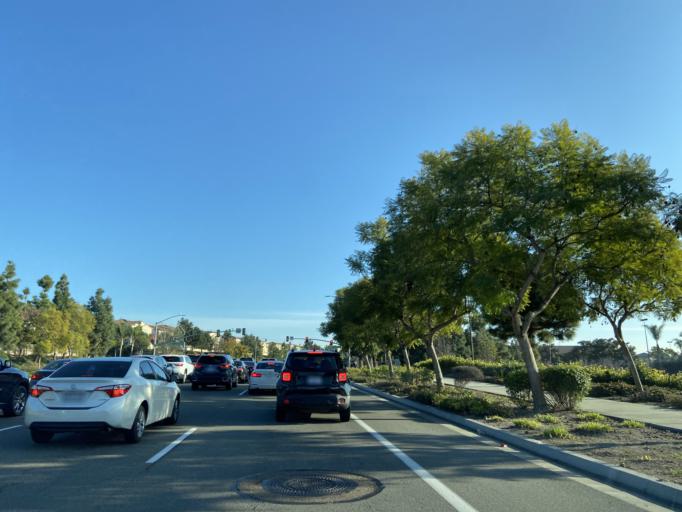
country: US
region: California
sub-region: San Diego County
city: Bonita
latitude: 32.6314
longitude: -116.9660
